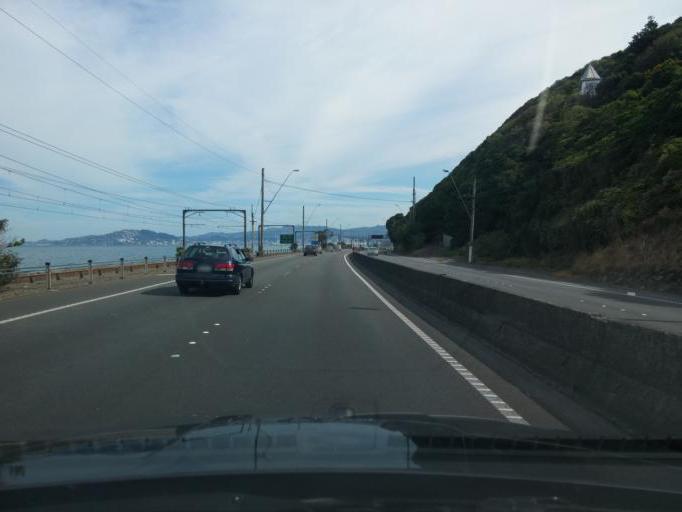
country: NZ
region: Wellington
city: Petone
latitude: -41.2342
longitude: 174.8353
